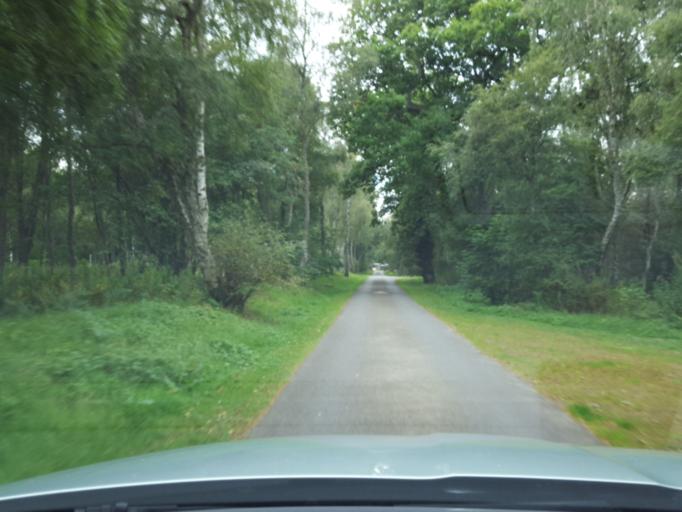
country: GB
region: Scotland
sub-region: Aberdeenshire
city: Alford
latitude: 57.2400
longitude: -2.6977
